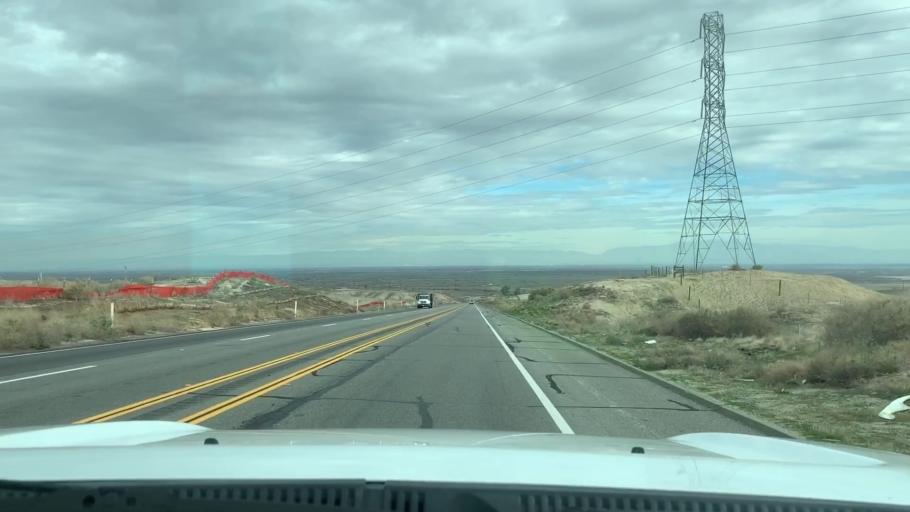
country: US
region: California
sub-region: Kern County
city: Ford City
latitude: 35.2589
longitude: -119.3243
